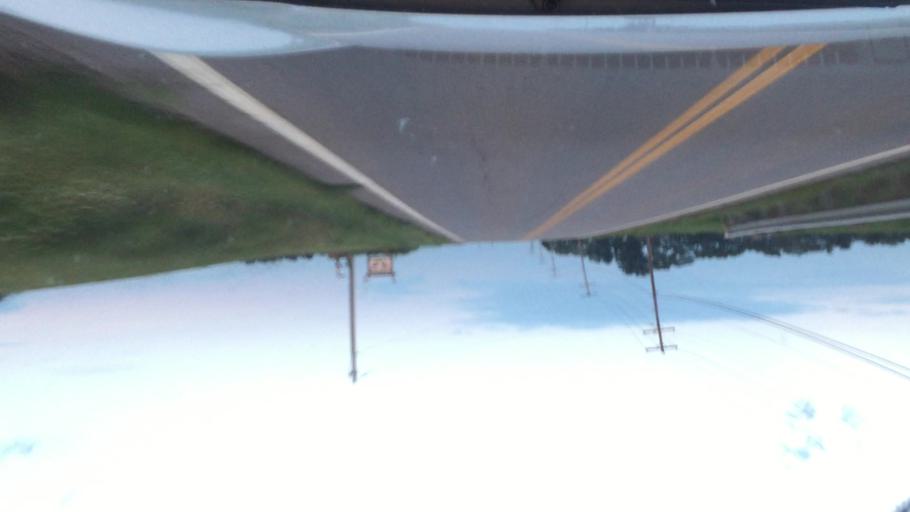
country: US
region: Ohio
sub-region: Madison County
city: West Jefferson
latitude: 39.9725
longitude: -83.3740
